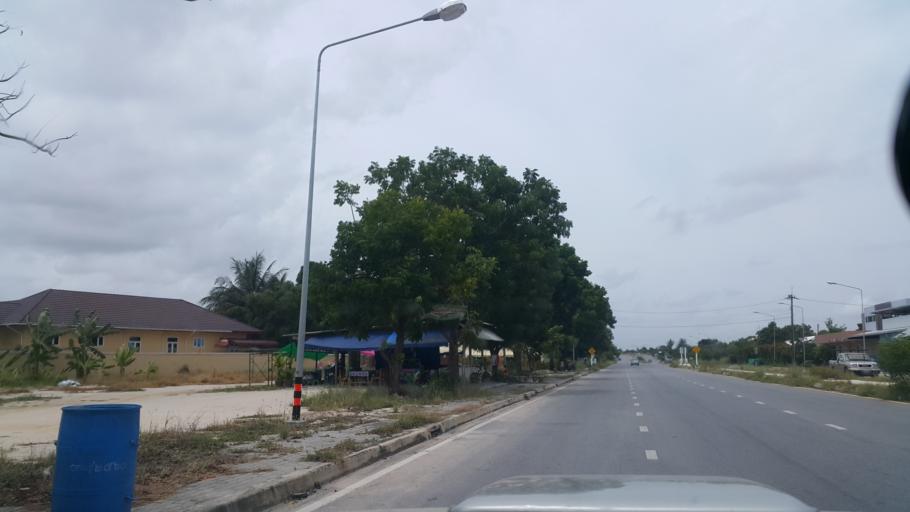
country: TH
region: Rayong
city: Ban Chang
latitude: 12.7156
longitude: 101.0632
